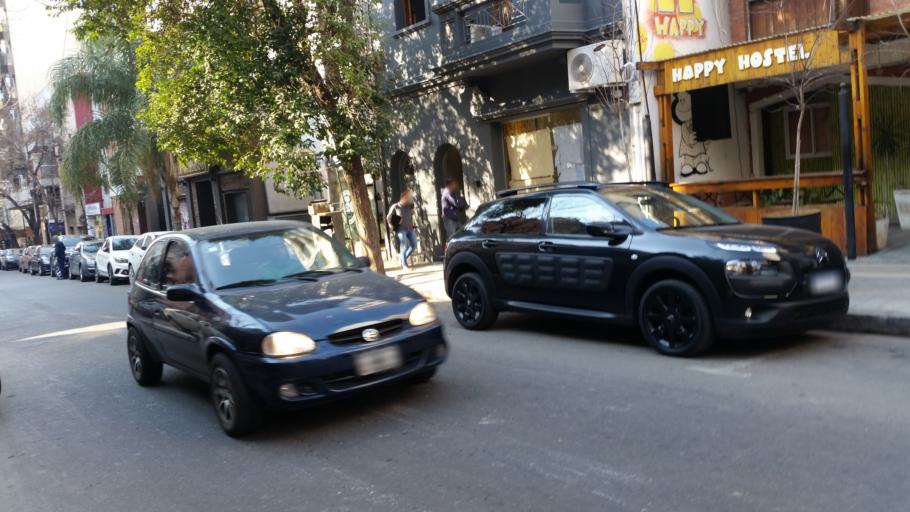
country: AR
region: Cordoba
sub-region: Departamento de Capital
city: Cordoba
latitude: -31.4283
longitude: -64.1892
